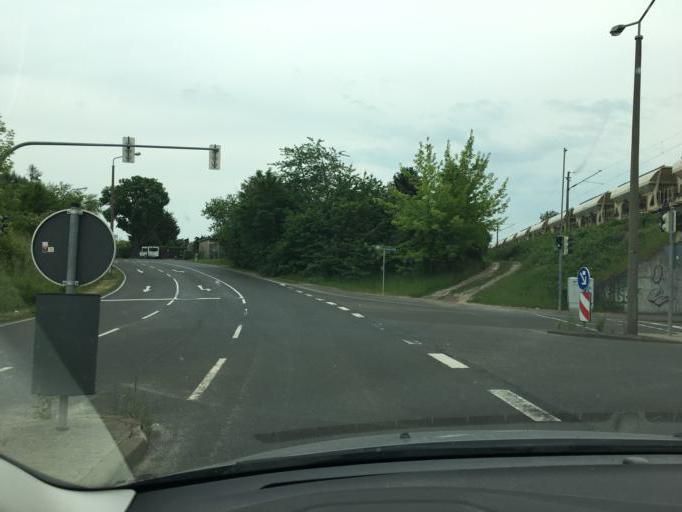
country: DE
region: Saxony
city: Taucha
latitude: 51.3675
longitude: 12.4419
